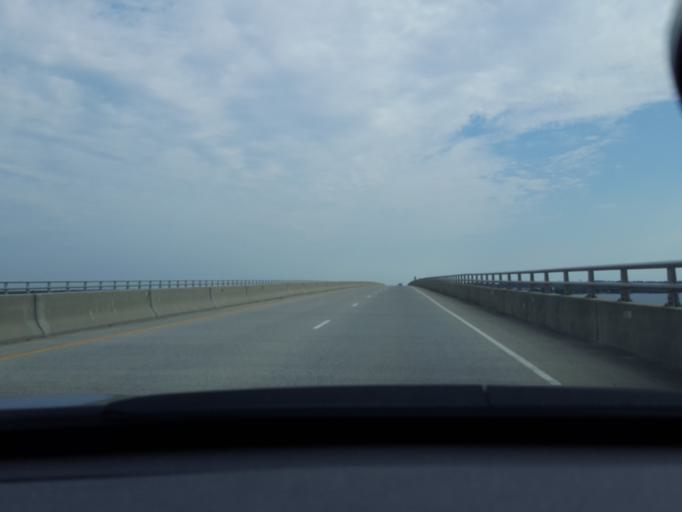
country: US
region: North Carolina
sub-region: Chowan County
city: Edenton
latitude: 36.0464
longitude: -76.6981
